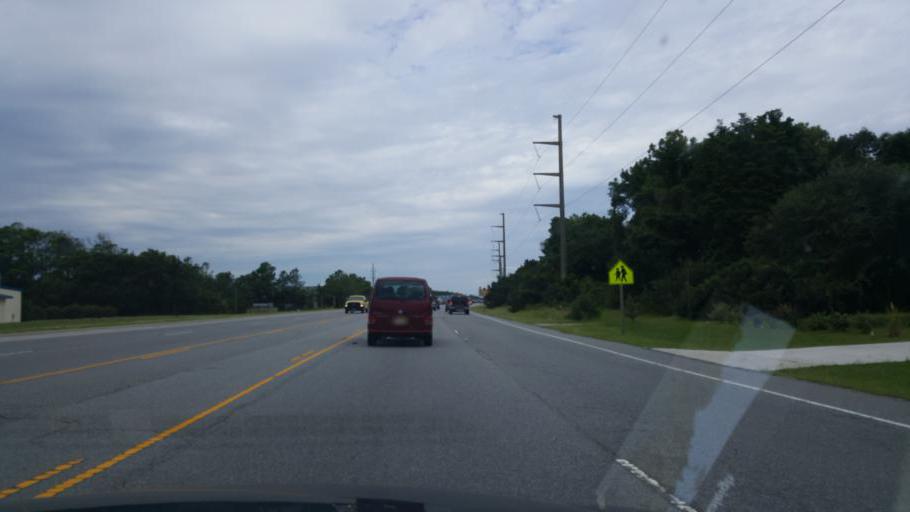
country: US
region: North Carolina
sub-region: Dare County
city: Nags Head
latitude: 35.9734
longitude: -75.6385
